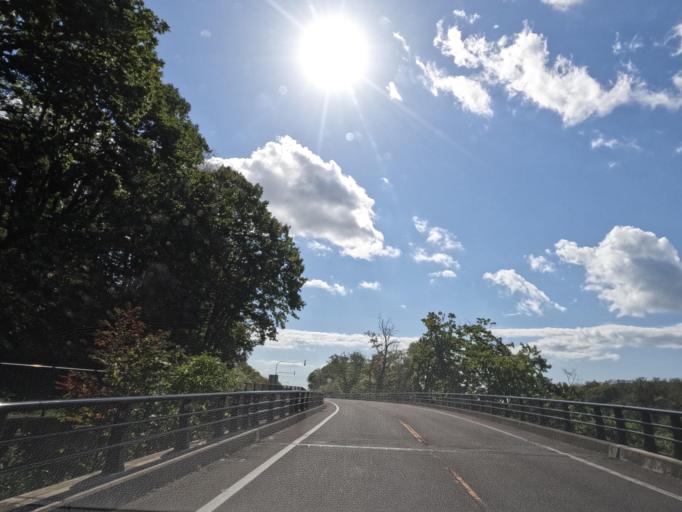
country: JP
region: Hokkaido
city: Shiraoi
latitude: 42.4790
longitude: 141.1458
